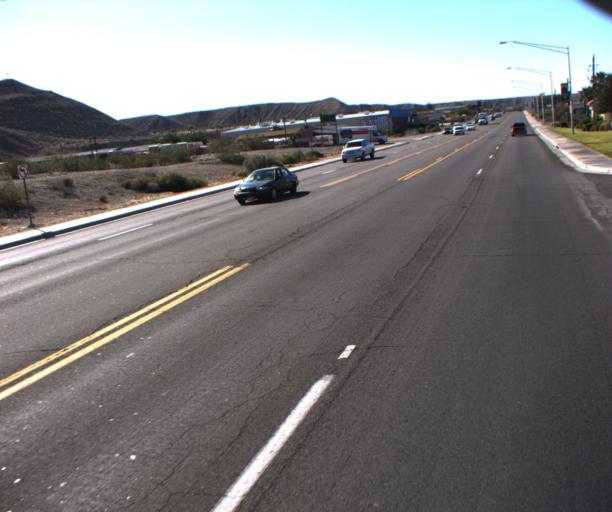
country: US
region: Arizona
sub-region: Mohave County
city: Bullhead City
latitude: 35.0760
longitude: -114.5930
